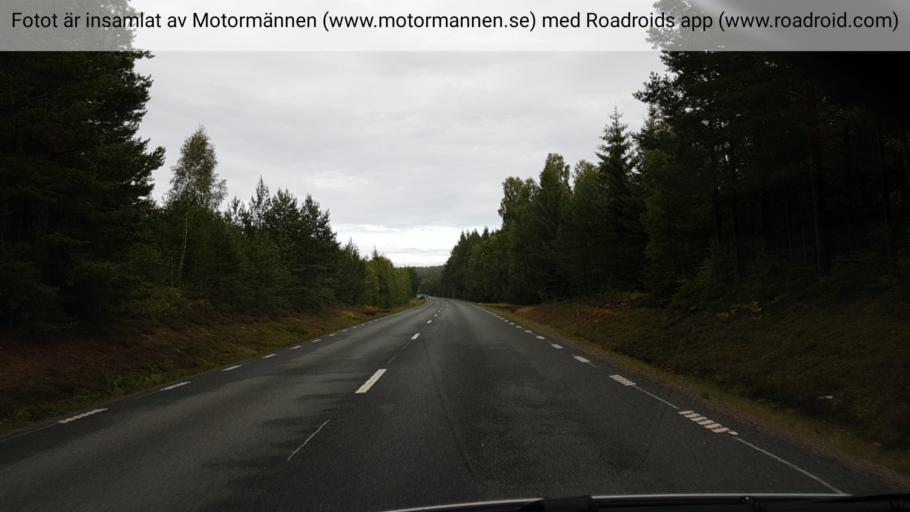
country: SE
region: Vaestra Goetaland
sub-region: Tidaholms Kommun
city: Olofstorp
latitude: 58.2177
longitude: 14.0937
